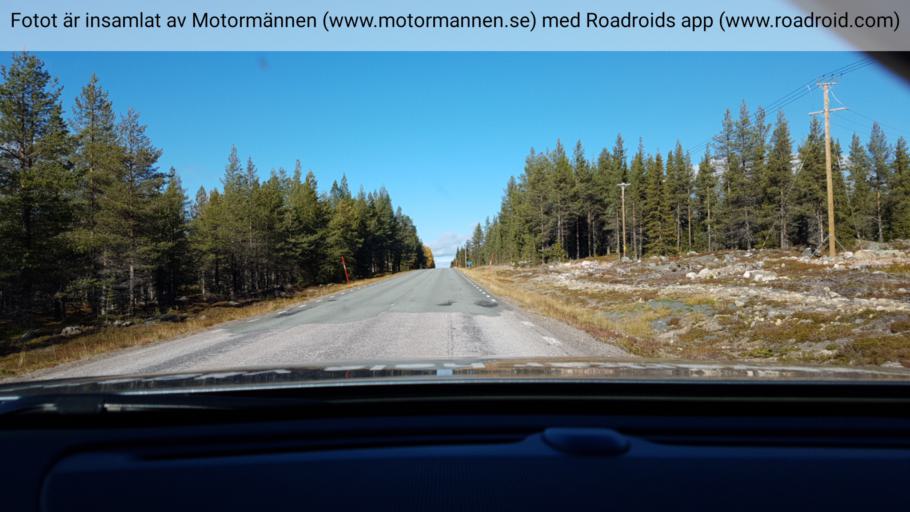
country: SE
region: Vaesterbotten
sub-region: Mala Kommun
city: Mala
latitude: 65.7848
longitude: 18.4964
